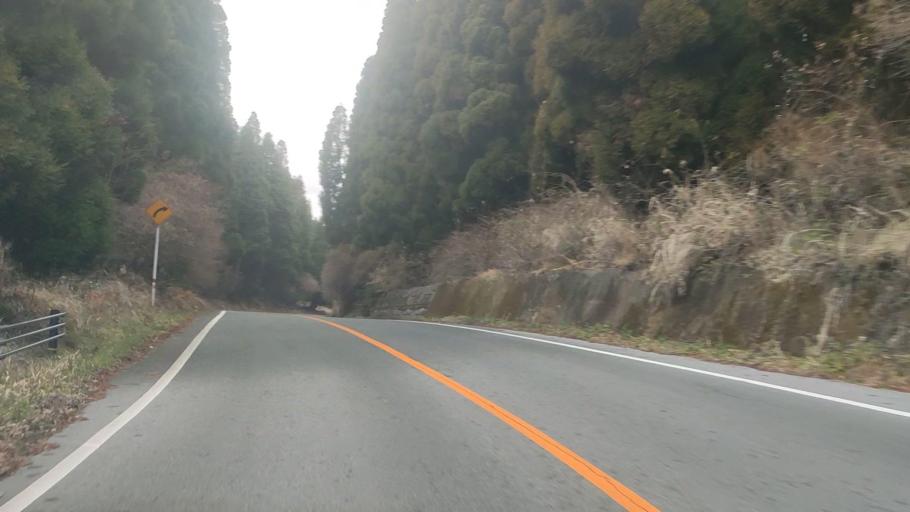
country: JP
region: Kumamoto
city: Aso
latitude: 32.9079
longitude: 131.1446
